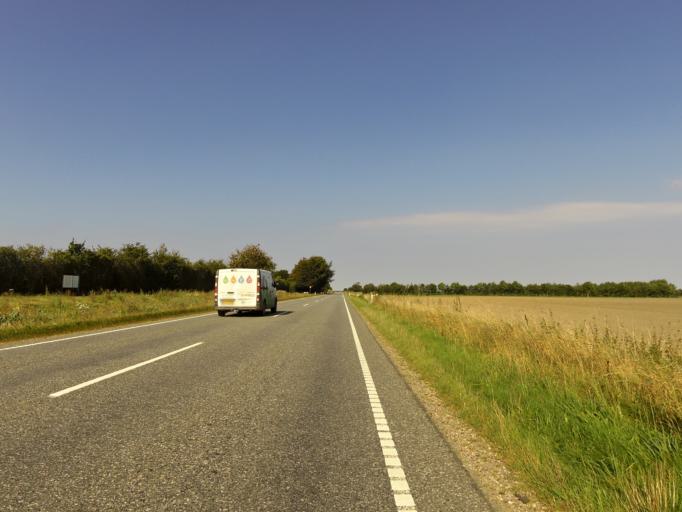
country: DK
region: South Denmark
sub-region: Vejen Kommune
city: Vejen
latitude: 55.3954
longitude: 9.1503
